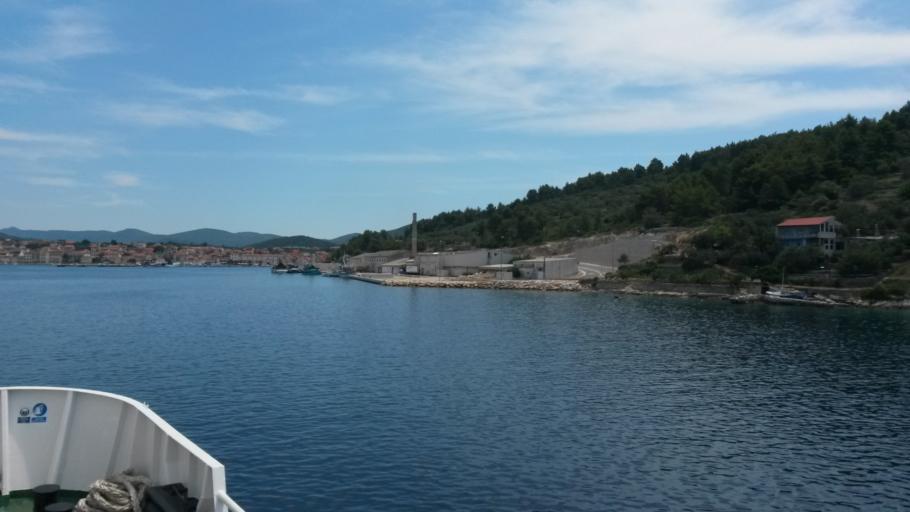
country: HR
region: Dubrovacko-Neretvanska
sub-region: Grad Dubrovnik
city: Vela Luka
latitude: 42.9615
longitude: 16.7010
